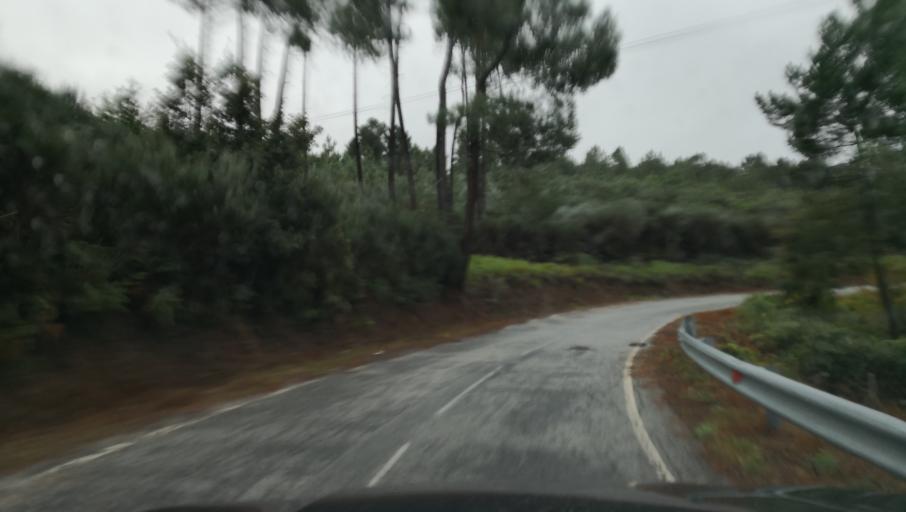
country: PT
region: Vila Real
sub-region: Sabrosa
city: Sabrosa
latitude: 41.3468
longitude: -7.5857
